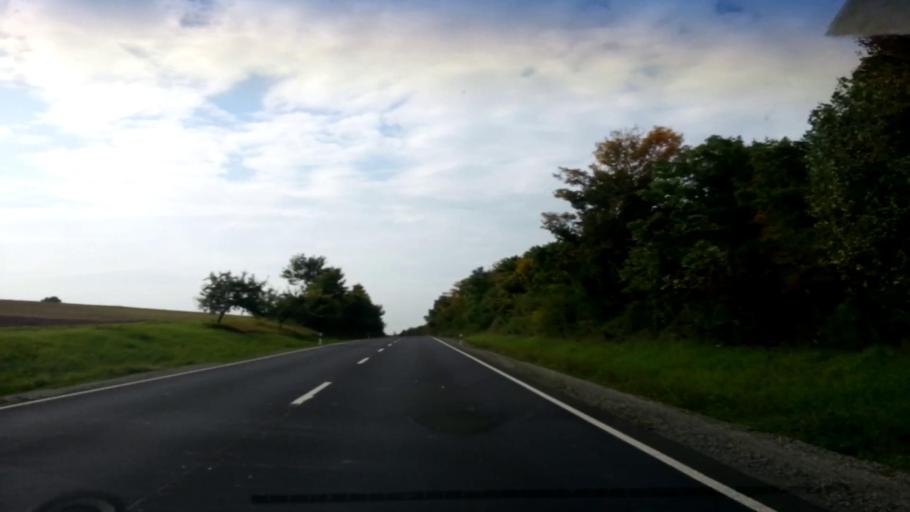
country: DE
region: Bavaria
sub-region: Regierungsbezirk Unterfranken
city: Gerolzhofen
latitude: 49.8956
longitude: 10.3599
